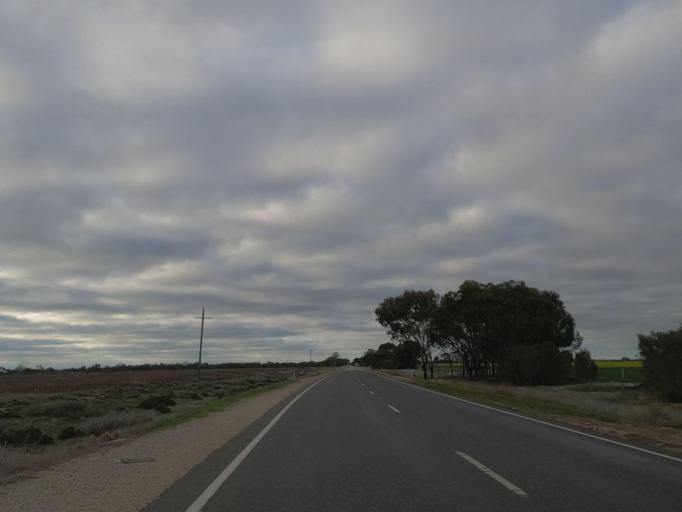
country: AU
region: Victoria
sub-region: Swan Hill
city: Swan Hill
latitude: -35.8279
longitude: 143.9457
